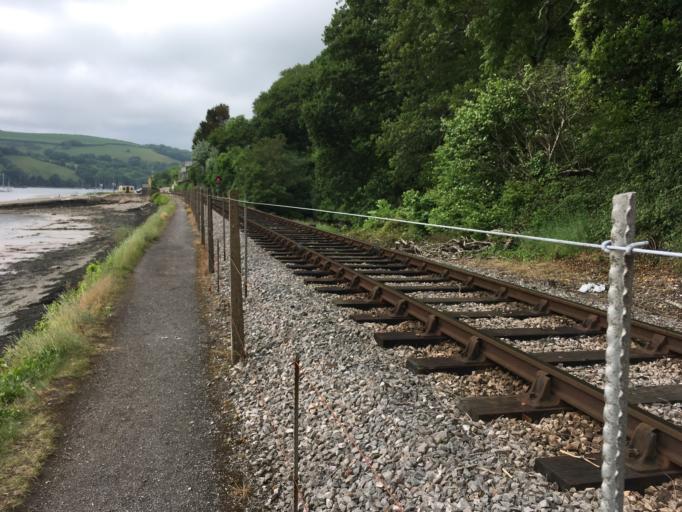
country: GB
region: England
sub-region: Devon
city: Dartmouth
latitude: 50.3585
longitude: -3.5718
